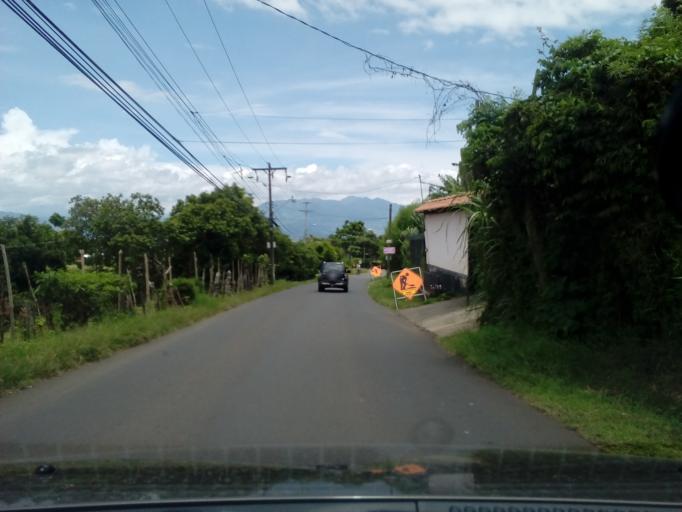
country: CR
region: Heredia
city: San Josecito
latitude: 10.0226
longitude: -84.0835
